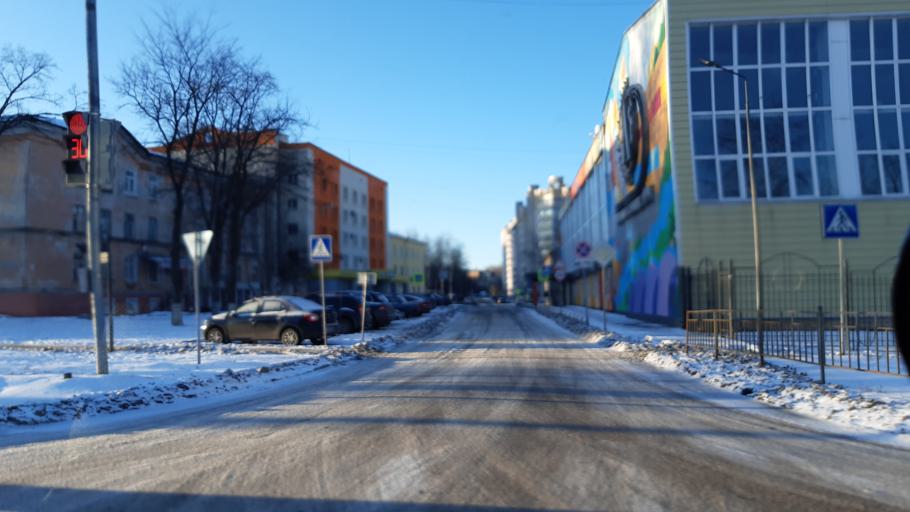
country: RU
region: Moskovskaya
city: Sergiyev Posad
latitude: 56.3247
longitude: 38.1472
